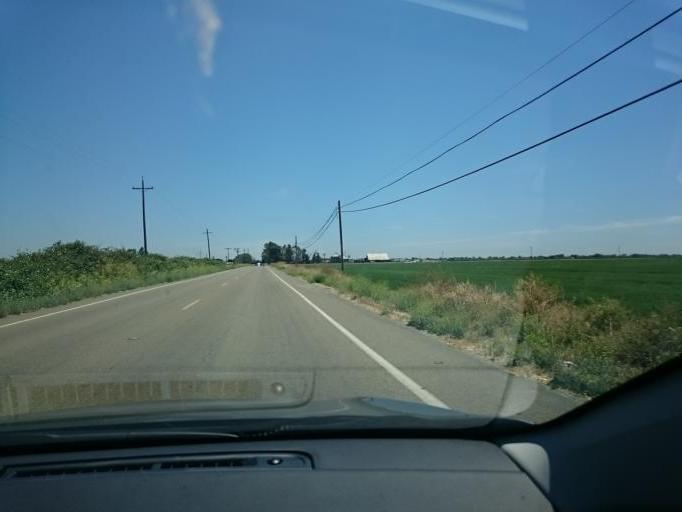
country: US
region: California
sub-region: Sacramento County
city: Walnut Grove
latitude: 38.2254
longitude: -121.4792
